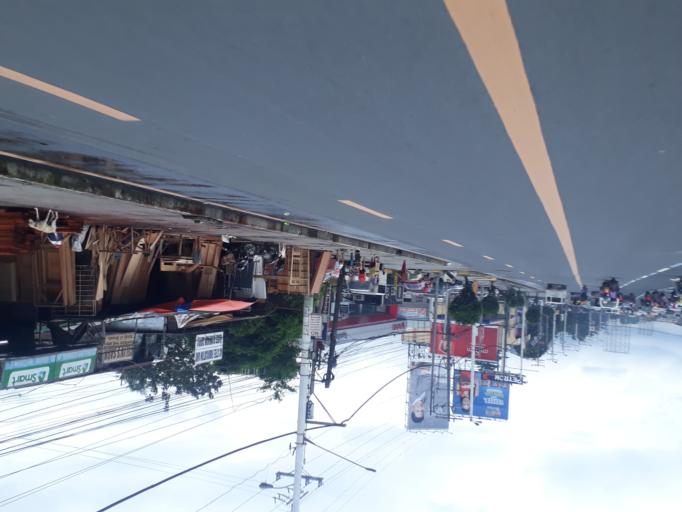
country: PH
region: Metro Manila
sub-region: Quezon City
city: Quezon City
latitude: 14.6690
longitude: 121.0763
